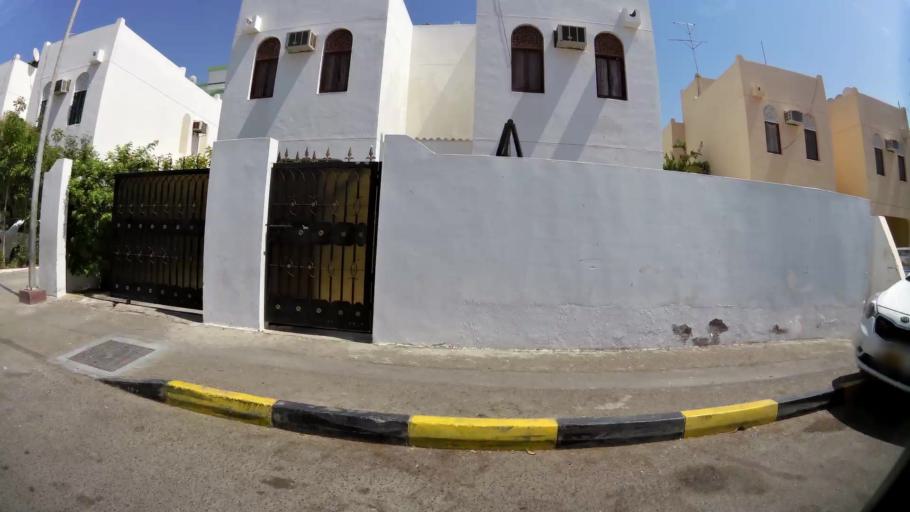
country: OM
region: Muhafazat Masqat
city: Muscat
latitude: 23.5726
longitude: 58.6100
